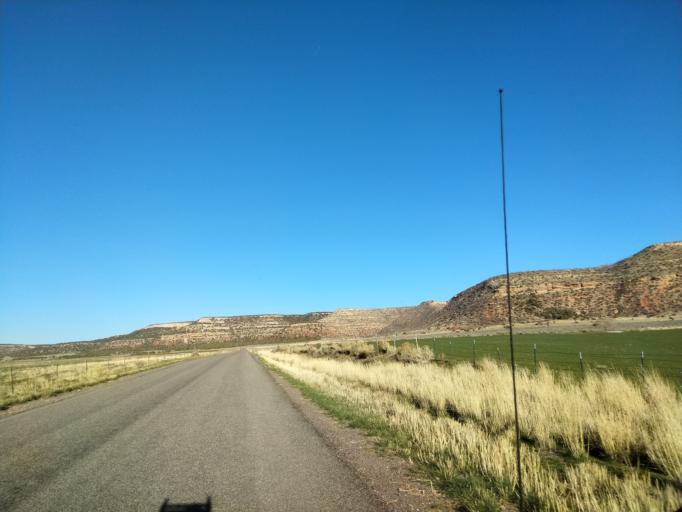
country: US
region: Colorado
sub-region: Mesa County
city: Loma
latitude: 38.9490
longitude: -109.0471
